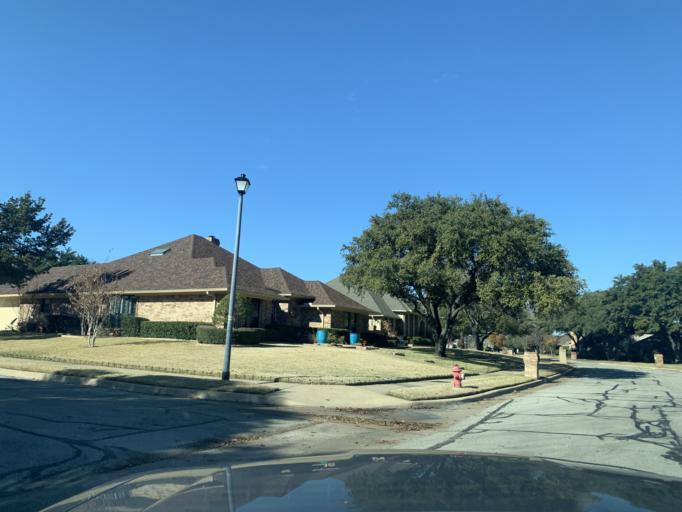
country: US
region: Texas
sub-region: Tarrant County
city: Bedford
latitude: 32.8469
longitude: -97.1544
